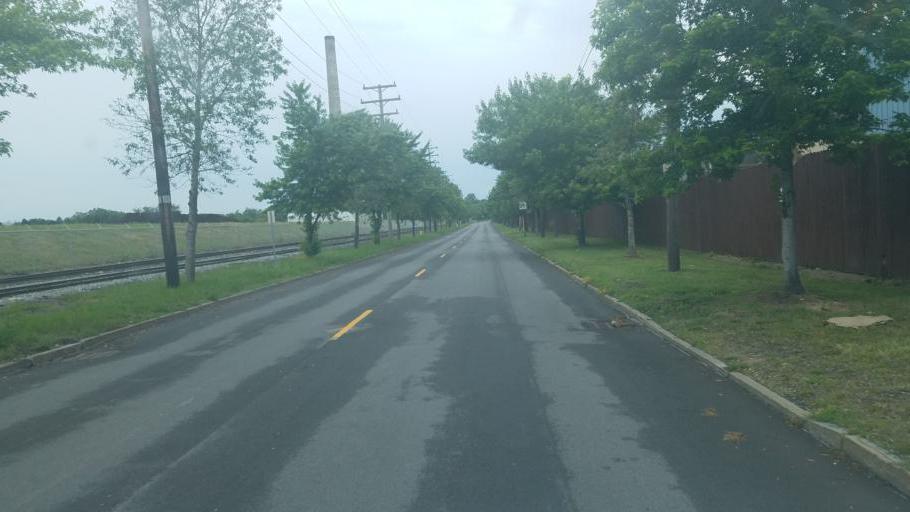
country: US
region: New York
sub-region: Niagara County
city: Niagara Falls
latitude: 43.1219
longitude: -79.0397
